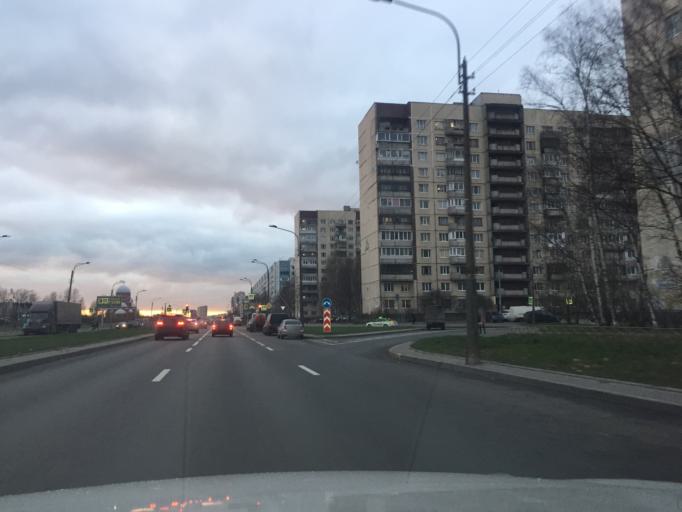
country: RU
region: St.-Petersburg
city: Grazhdanka
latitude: 60.0229
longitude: 30.4208
